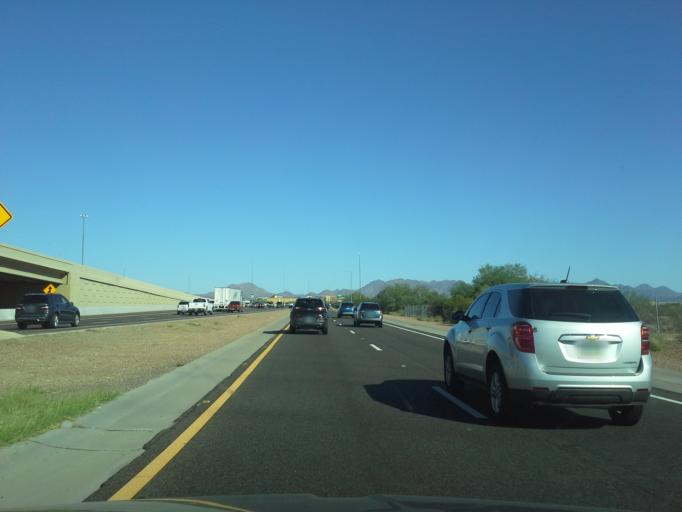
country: US
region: Arizona
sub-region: Maricopa County
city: Paradise Valley
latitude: 33.6717
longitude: -111.9961
